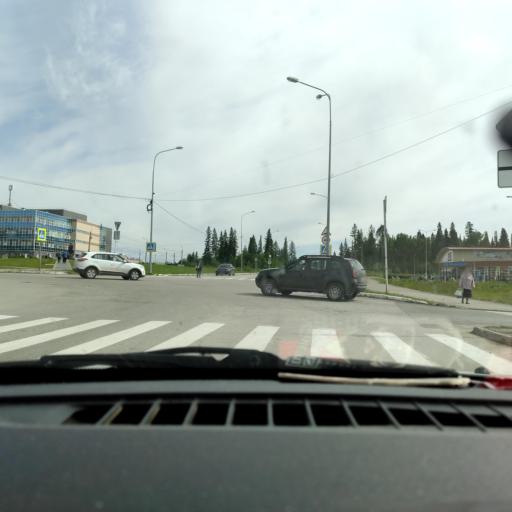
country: RU
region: Perm
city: Chusovoy
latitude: 58.2714
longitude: 57.8009
